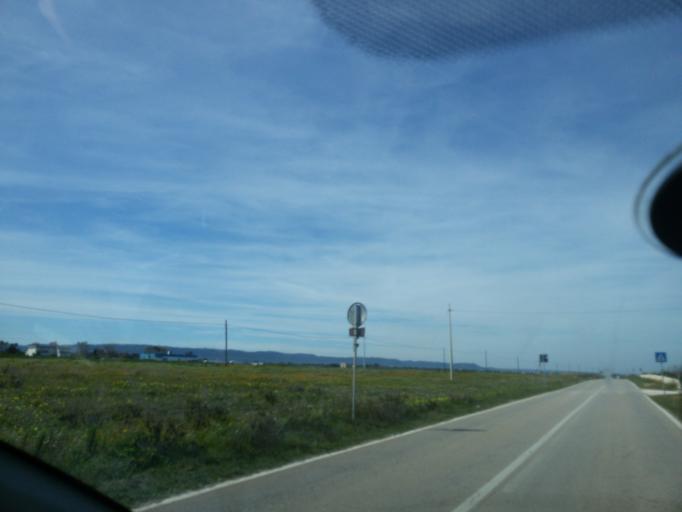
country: IT
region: Apulia
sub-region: Provincia di Brindisi
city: Pezze di Greco
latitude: 40.8473
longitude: 17.4565
